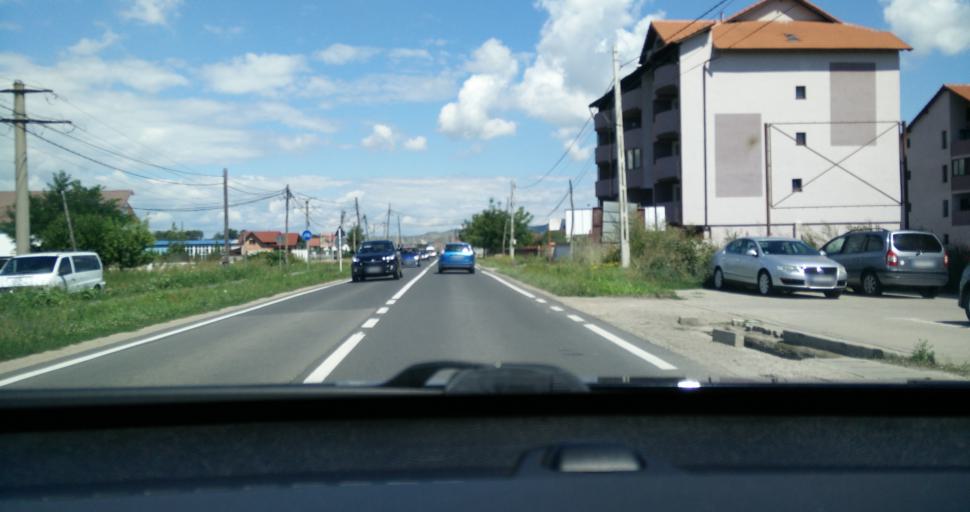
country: RO
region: Alba
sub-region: Municipiul Sebes
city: Petresti
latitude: 45.9374
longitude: 23.5624
